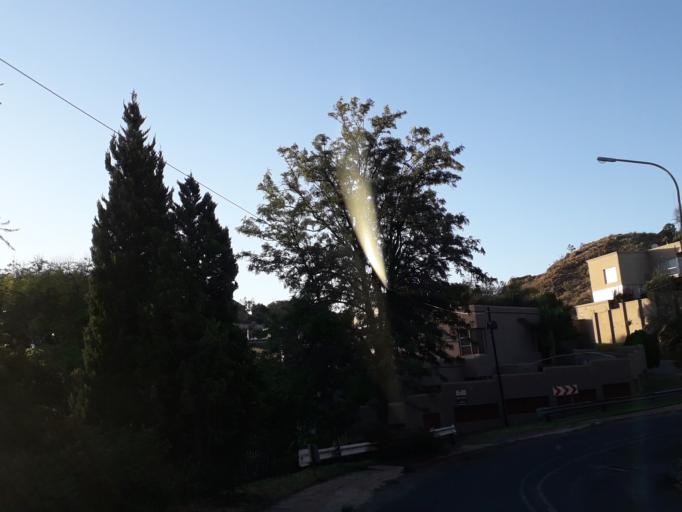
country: ZA
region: Gauteng
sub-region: City of Johannesburg Metropolitan Municipality
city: Roodepoort
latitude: -26.1580
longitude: 27.9335
